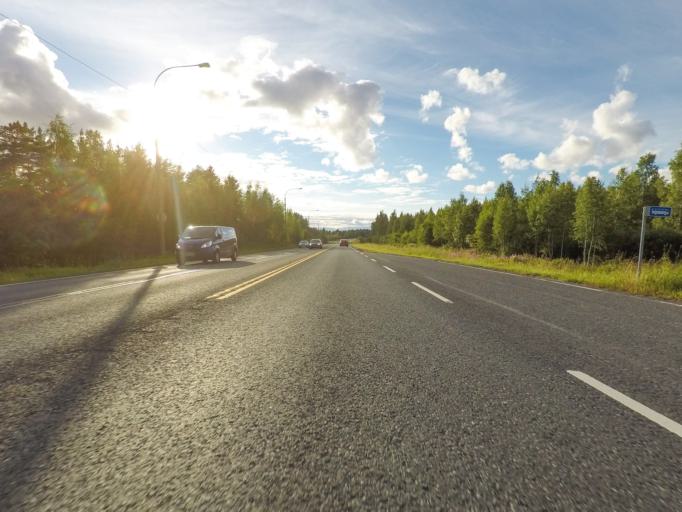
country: FI
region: Northern Savo
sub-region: Kuopio
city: Kuopio
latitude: 62.9569
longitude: 27.8648
